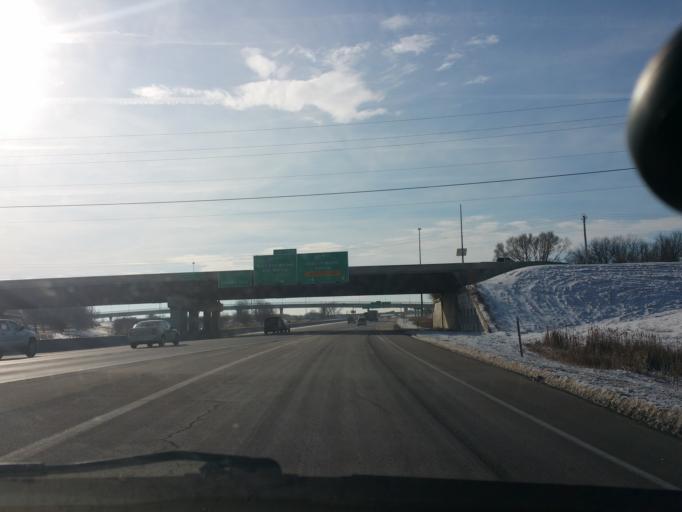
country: US
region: Iowa
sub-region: Polk County
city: Clive
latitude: 41.6015
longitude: -93.7771
